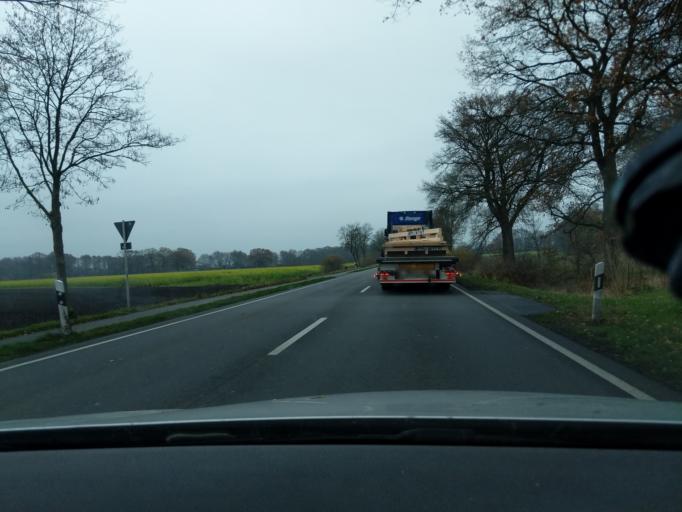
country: DE
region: Lower Saxony
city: Zeven
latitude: 53.2736
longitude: 9.2759
